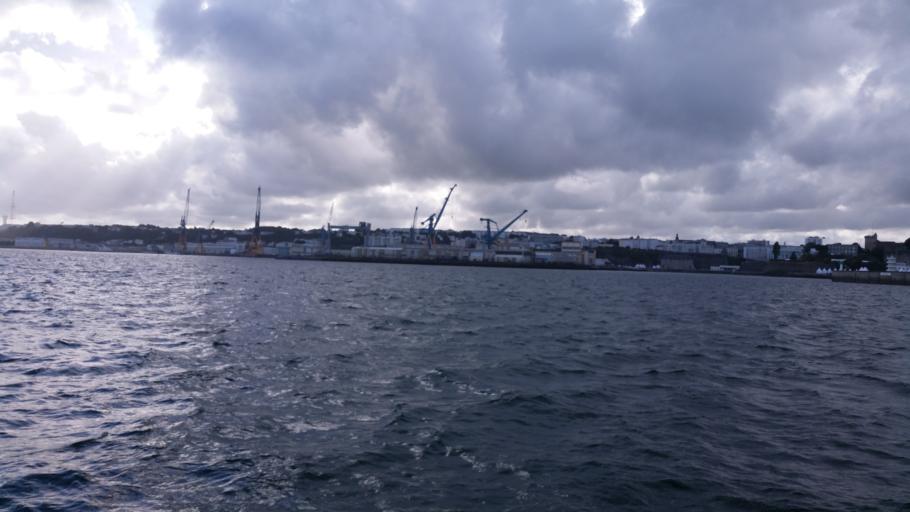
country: FR
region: Brittany
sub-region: Departement du Finistere
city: Brest
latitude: 48.3748
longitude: -4.4882
